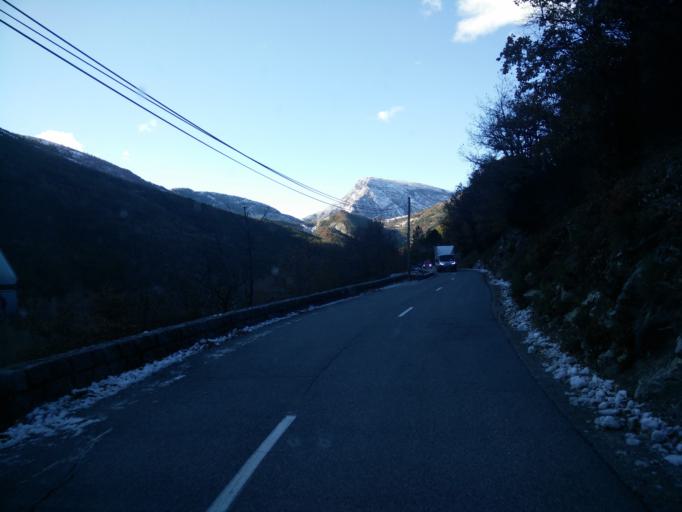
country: FR
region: Provence-Alpes-Cote d'Azur
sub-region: Departement des Alpes-de-Haute-Provence
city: Castellane
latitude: 43.8320
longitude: 6.4782
